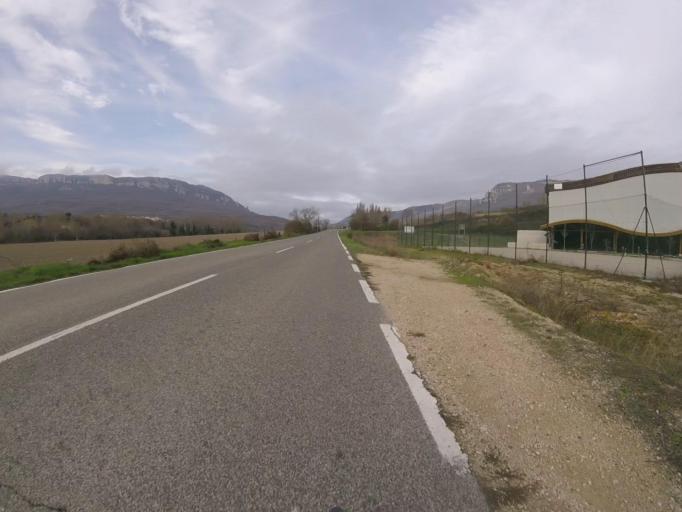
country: ES
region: Navarre
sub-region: Provincia de Navarra
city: Estella
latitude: 42.7167
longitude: -2.0747
